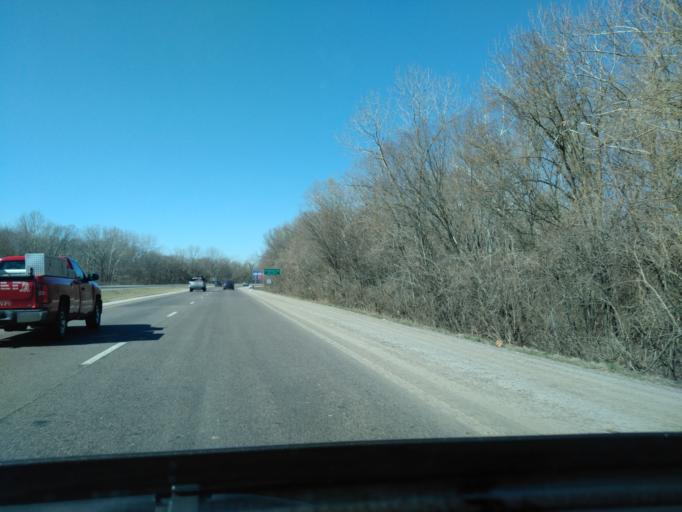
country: US
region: Missouri
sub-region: Saint Louis County
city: Fenton
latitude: 38.5181
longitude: -90.4239
